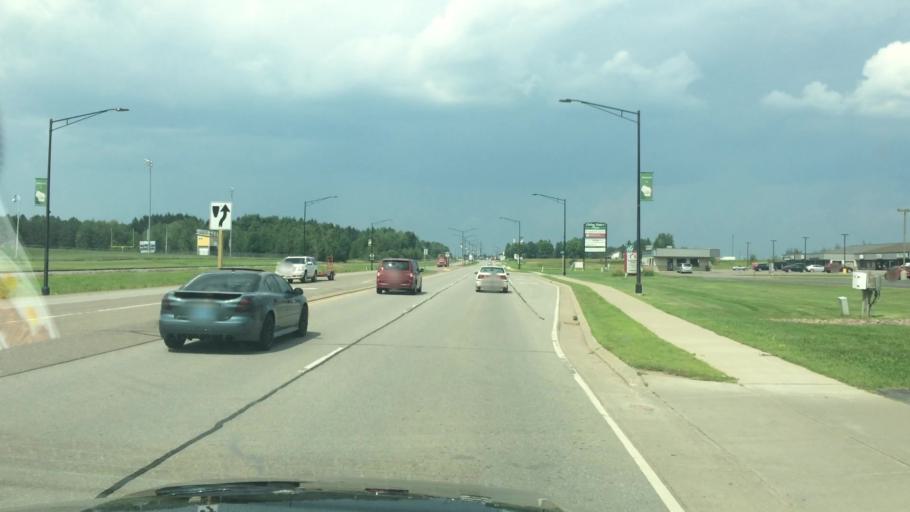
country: US
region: Wisconsin
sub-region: Clark County
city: Colby
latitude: 44.9182
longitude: -90.3153
